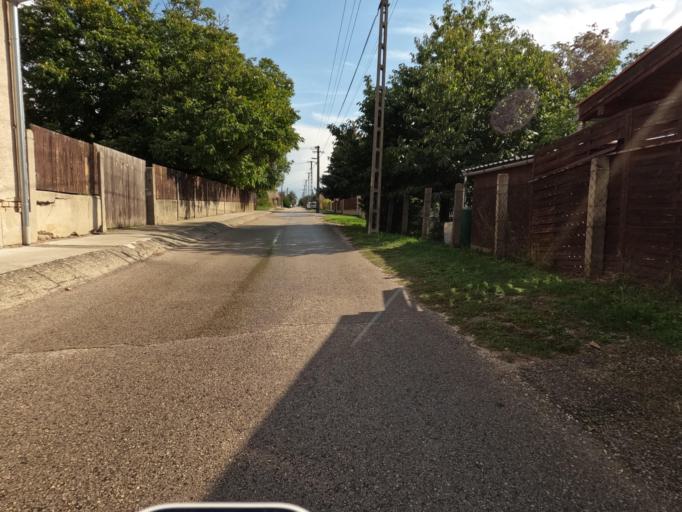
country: HU
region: Tolna
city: Tengelic
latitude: 46.5265
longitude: 18.7074
